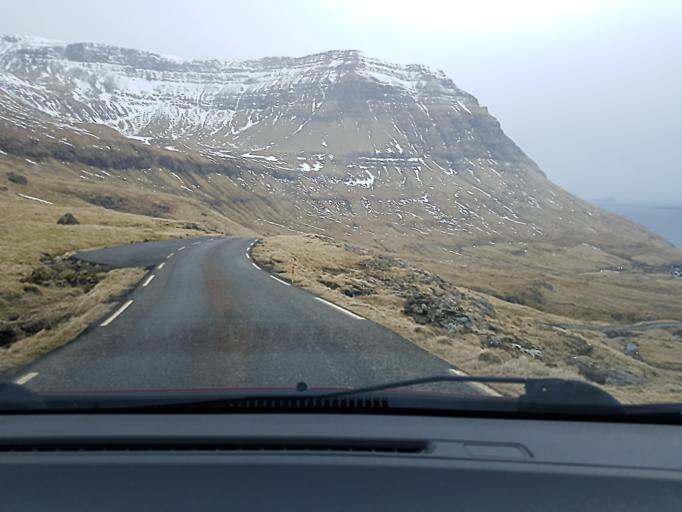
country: FO
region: Streymoy
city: Kollafjordhur
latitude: 62.0479
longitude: -6.9230
